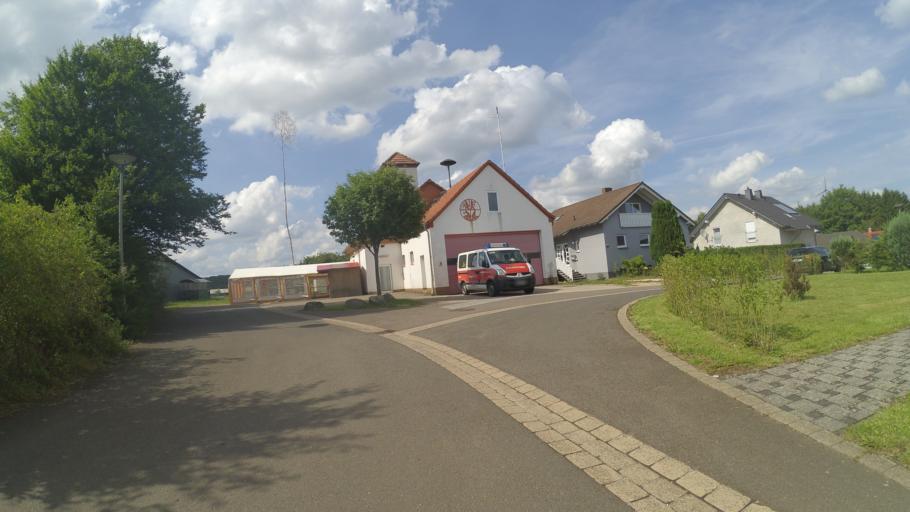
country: DE
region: Rheinland-Pfalz
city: Achtelsbach
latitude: 49.5963
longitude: 7.0648
